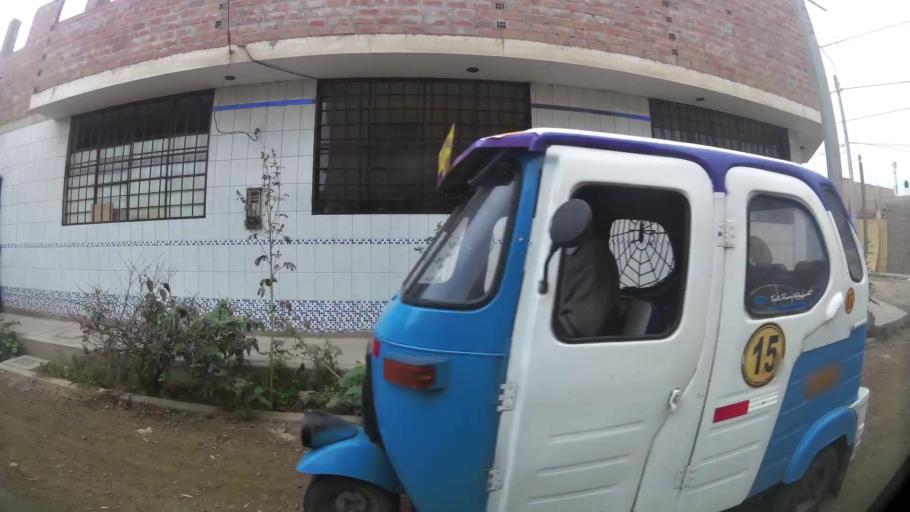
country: PE
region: Lima
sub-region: Provincia de Huaral
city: Huaral
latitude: -11.5010
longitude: -77.2087
